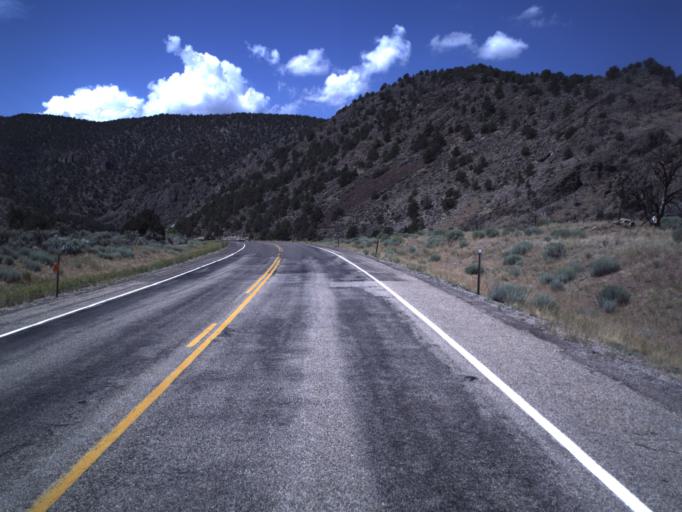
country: US
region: Utah
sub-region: Piute County
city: Junction
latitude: 38.1258
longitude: -112.3292
